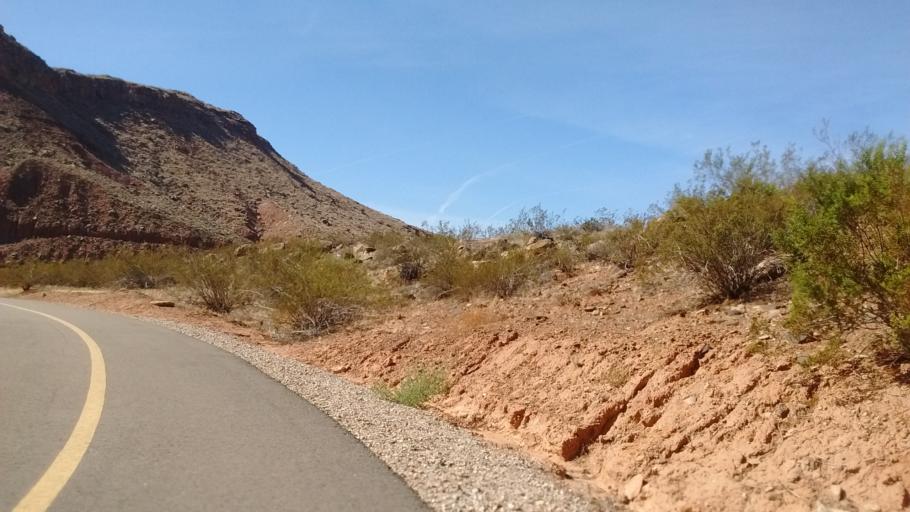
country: US
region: Utah
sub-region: Washington County
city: Washington
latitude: 37.1242
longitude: -113.4856
